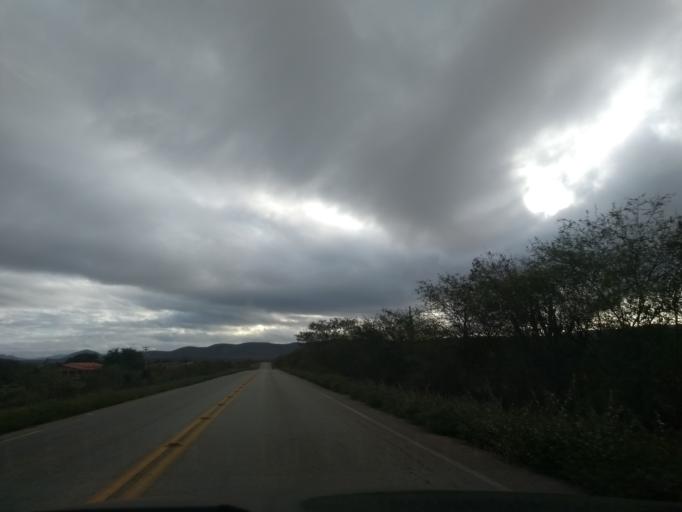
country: BR
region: Bahia
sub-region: Ituacu
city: Ituacu
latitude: -13.7576
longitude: -41.0303
